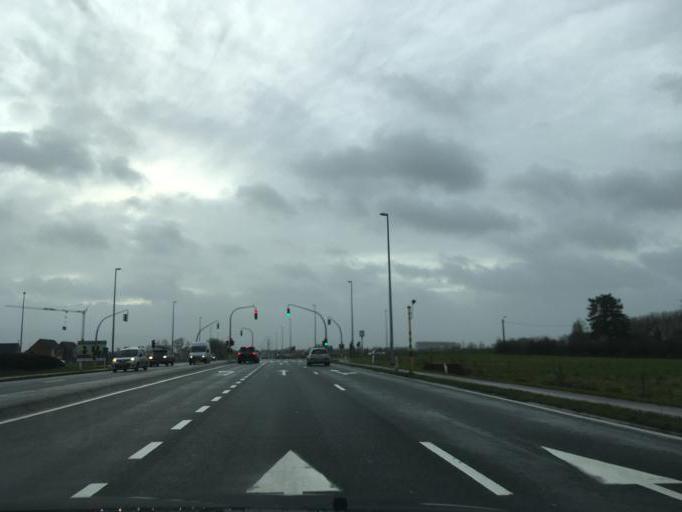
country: BE
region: Flanders
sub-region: Provincie West-Vlaanderen
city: Roeselare
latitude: 50.9400
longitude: 3.0990
